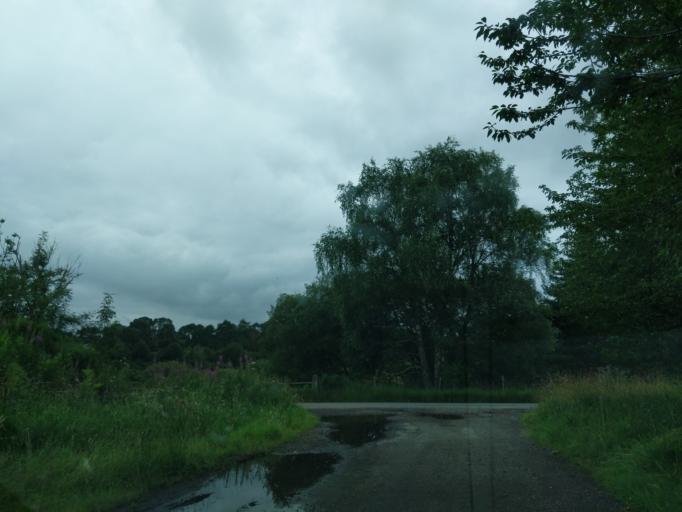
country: GB
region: Scotland
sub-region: Moray
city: Kinloss
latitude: 57.5710
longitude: -3.5301
